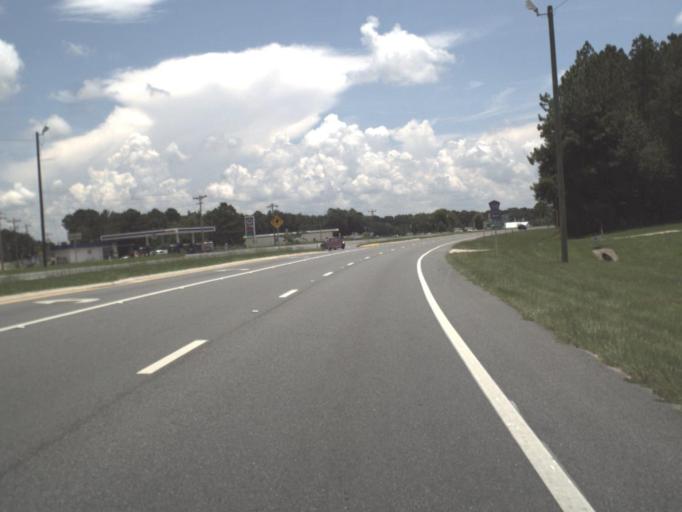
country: US
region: Florida
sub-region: Levy County
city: Williston
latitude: 29.3883
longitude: -82.4318
